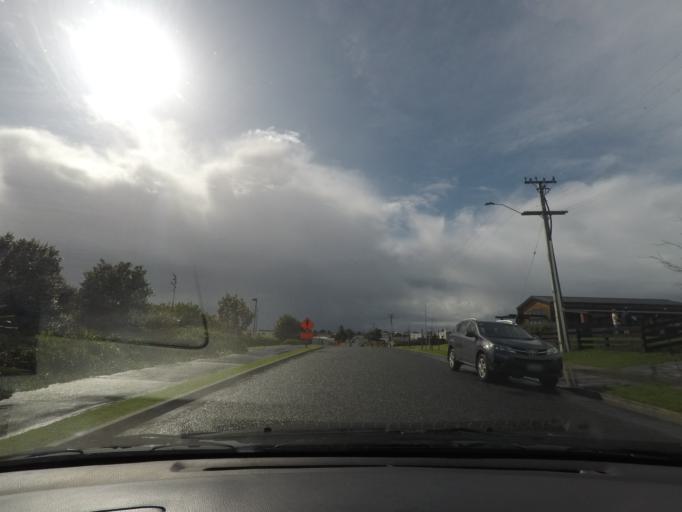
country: NZ
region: Auckland
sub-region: Auckland
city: Warkworth
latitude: -36.4292
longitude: 174.7241
